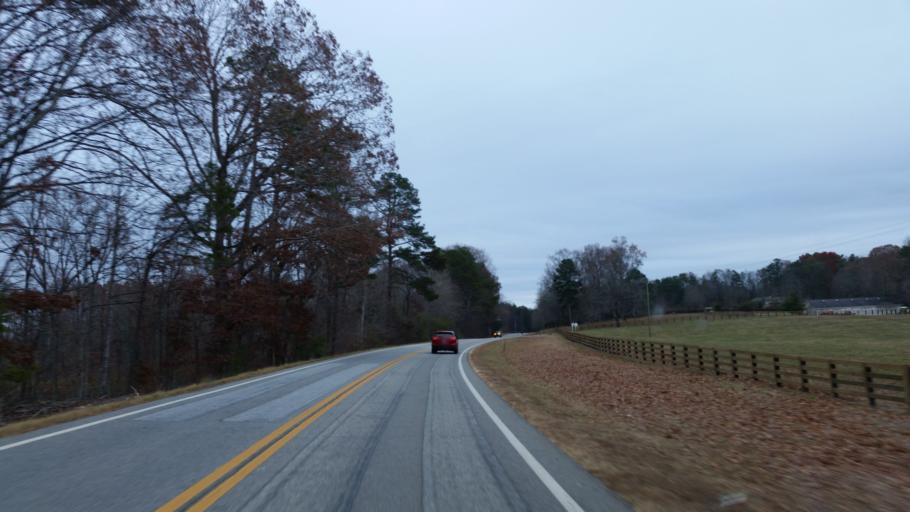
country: US
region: Georgia
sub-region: Dawson County
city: Dawsonville
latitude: 34.4410
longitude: -84.0873
